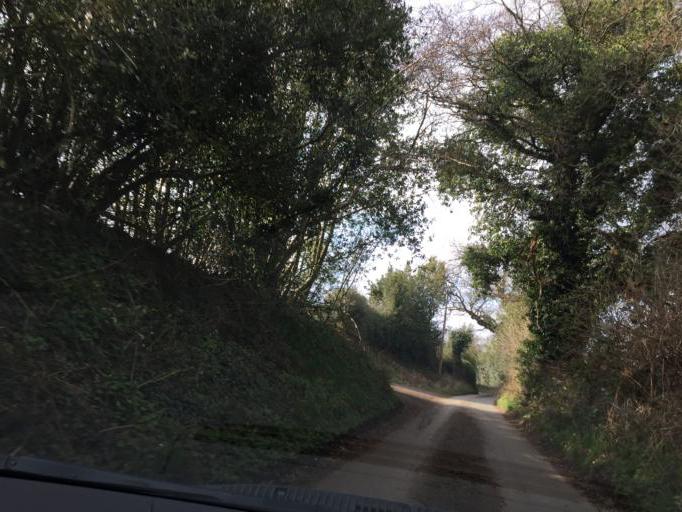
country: GB
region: England
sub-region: Solihull
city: Meriden
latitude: 52.4465
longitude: -1.5936
